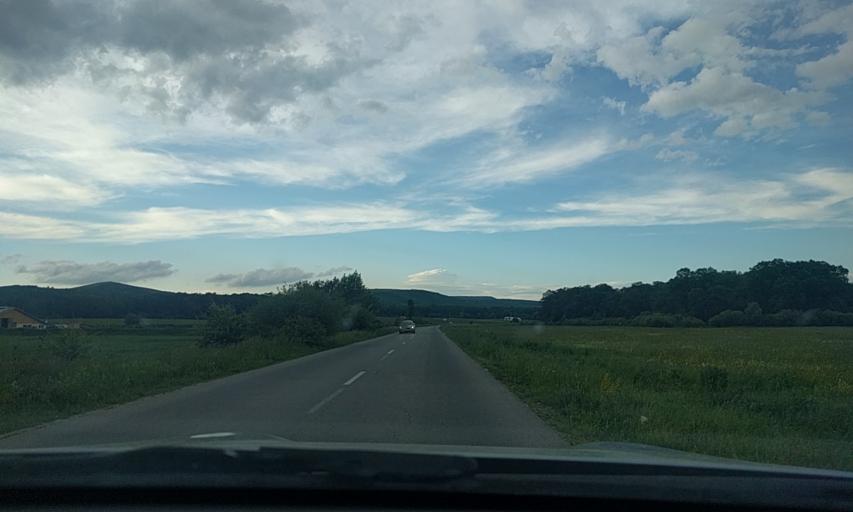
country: RO
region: Brasov
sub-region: Comuna Harman
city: Harman
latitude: 45.7430
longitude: 25.7040
